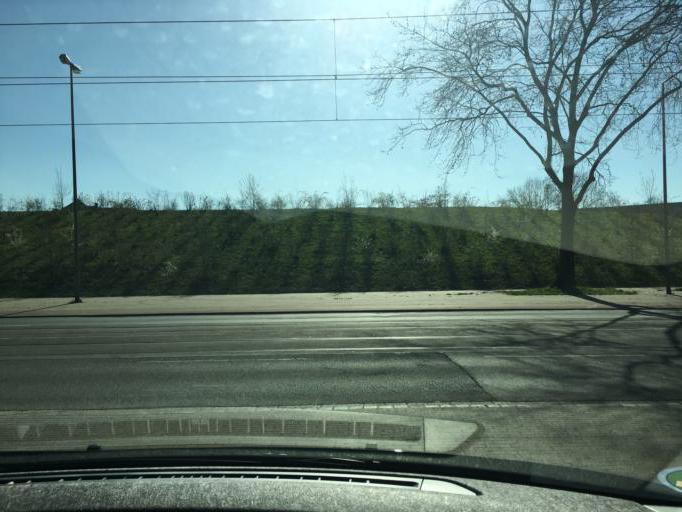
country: DE
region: North Rhine-Westphalia
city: Meiderich
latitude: 51.4891
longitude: 6.7387
